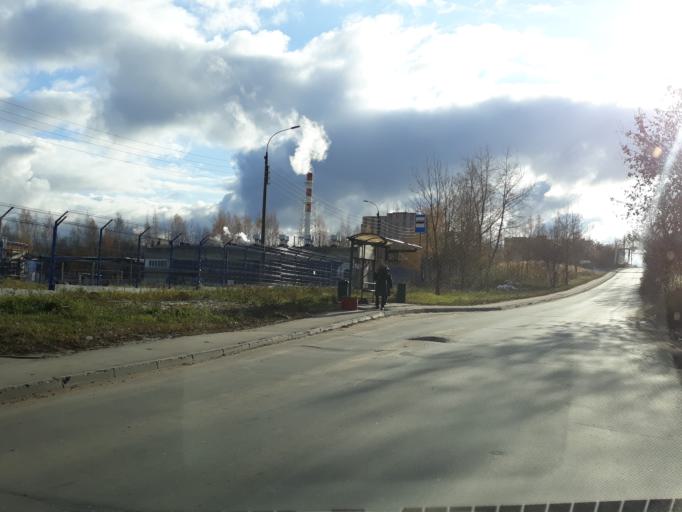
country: RU
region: Nizjnij Novgorod
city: Afonino
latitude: 56.2372
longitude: 44.0075
